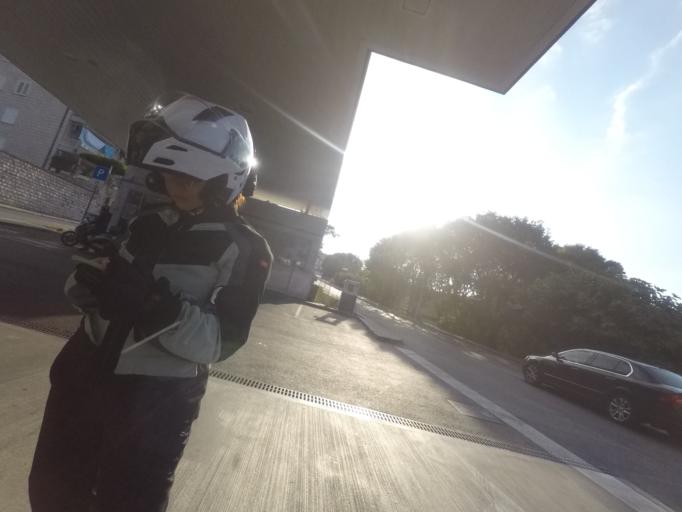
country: HR
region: Dubrovacko-Neretvanska
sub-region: Grad Dubrovnik
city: Dubrovnik
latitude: 42.6488
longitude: 18.0948
